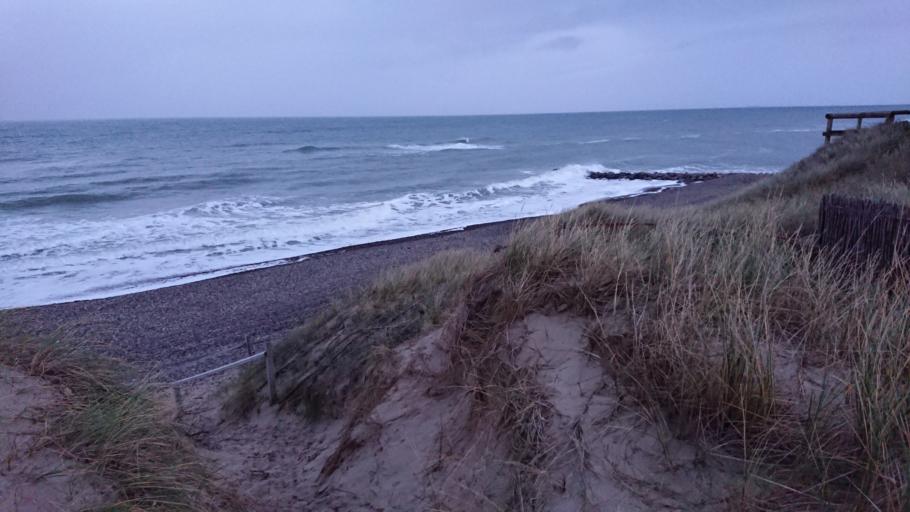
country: DK
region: North Denmark
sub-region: Frederikshavn Kommune
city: Skagen
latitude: 57.7298
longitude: 10.5232
